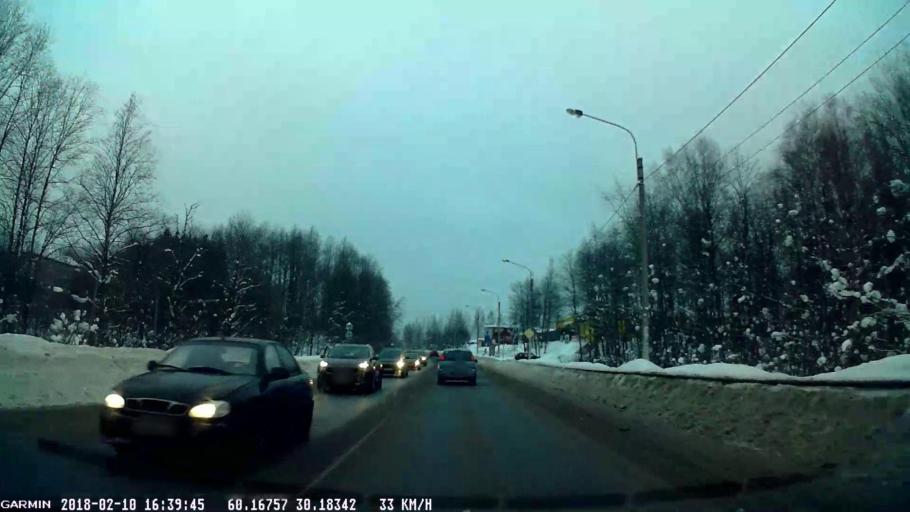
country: RU
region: Leningrad
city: Sertolovo
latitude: 60.1582
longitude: 30.1874
